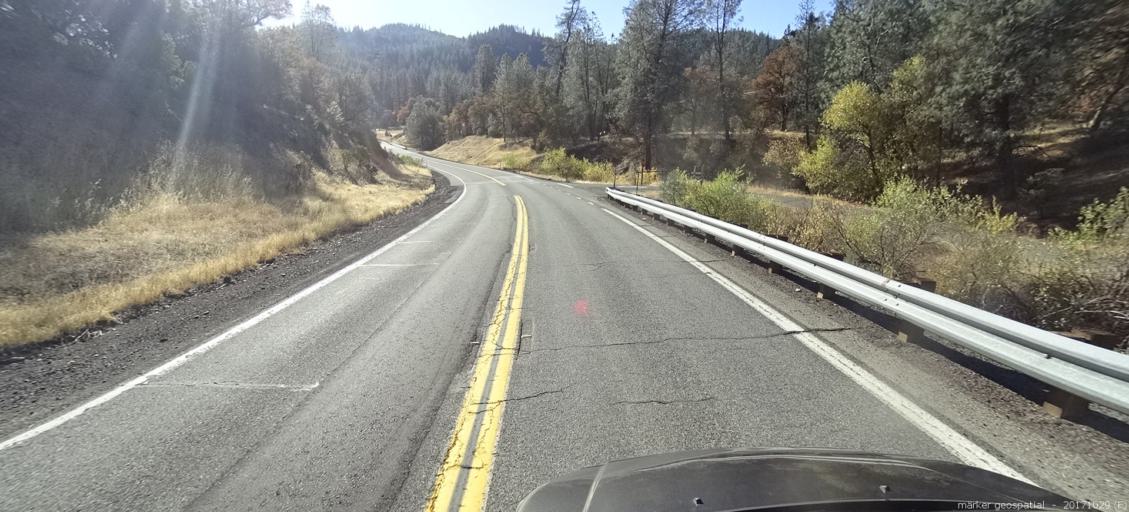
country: US
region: California
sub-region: Trinity County
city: Hayfork
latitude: 40.3618
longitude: -122.9121
